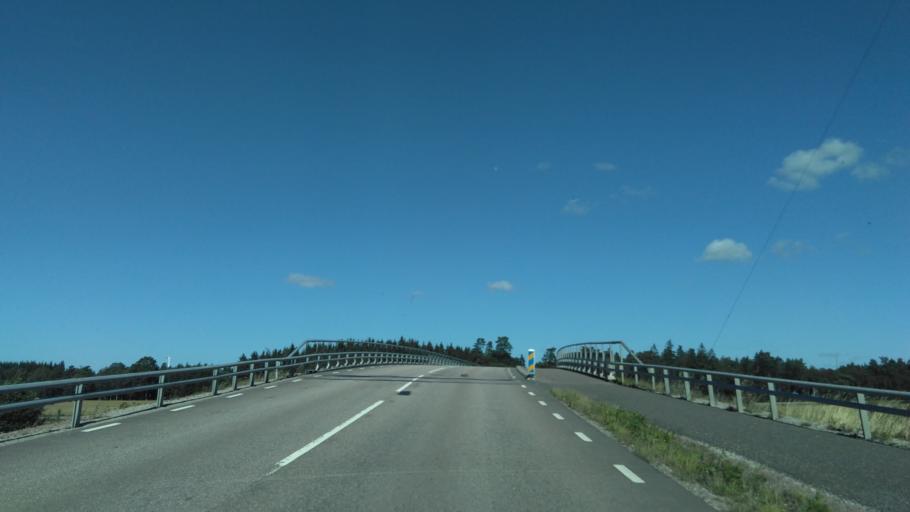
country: SE
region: Vaestra Goetaland
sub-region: Skara Kommun
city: Axvall
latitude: 58.3947
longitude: 13.5313
